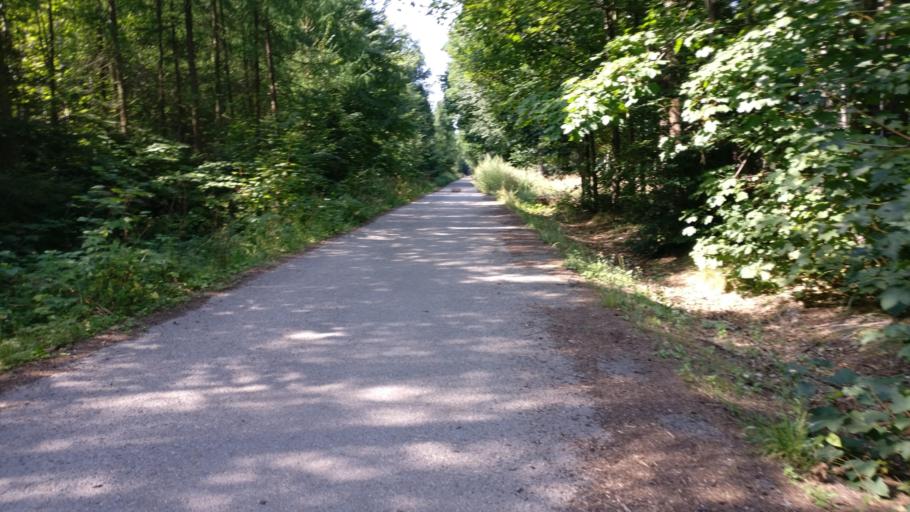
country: CZ
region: South Moravian
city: Zbraslav
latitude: 49.2127
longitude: 16.2781
